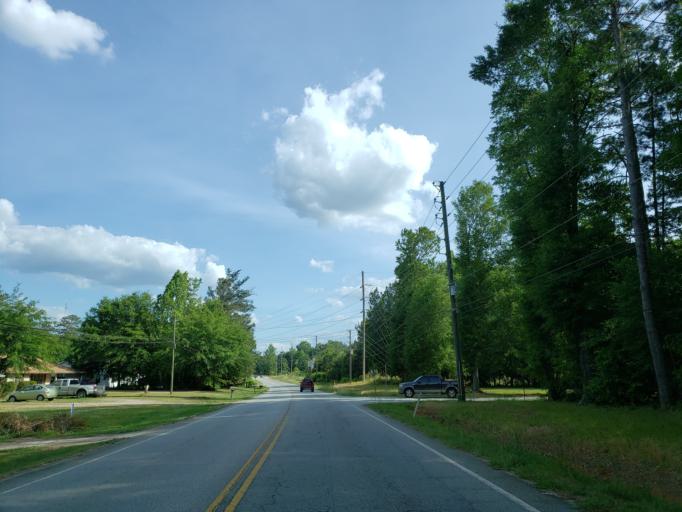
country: US
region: Georgia
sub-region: Carroll County
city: Carrollton
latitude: 33.6103
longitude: -85.0809
